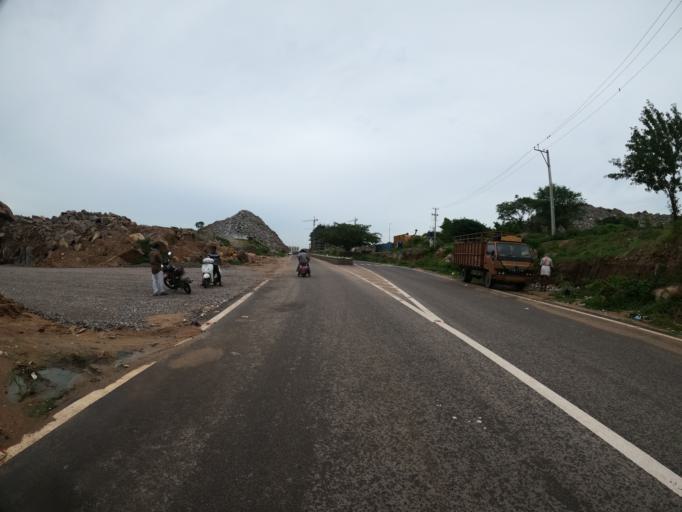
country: IN
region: Telangana
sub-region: Rangareddi
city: Kukatpalli
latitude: 17.4639
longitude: 78.3791
